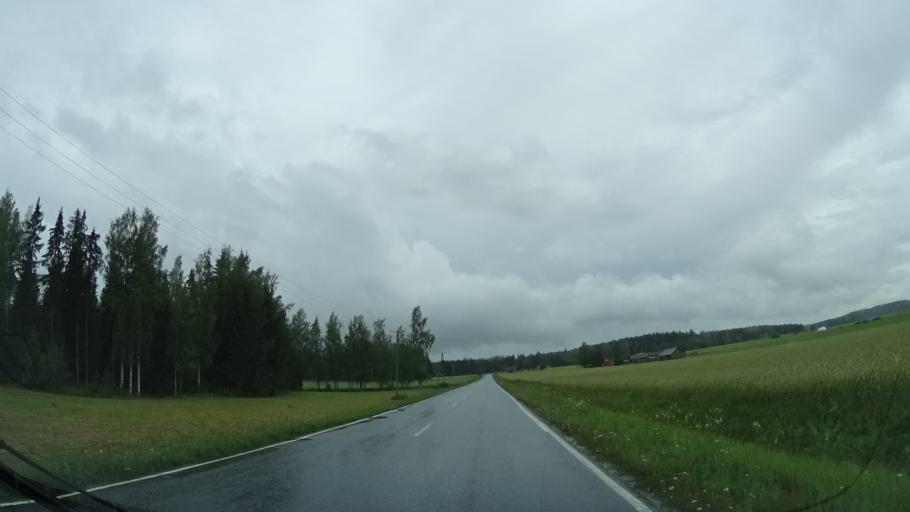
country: FI
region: Haeme
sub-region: Forssa
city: Humppila
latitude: 60.9817
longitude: 23.2533
